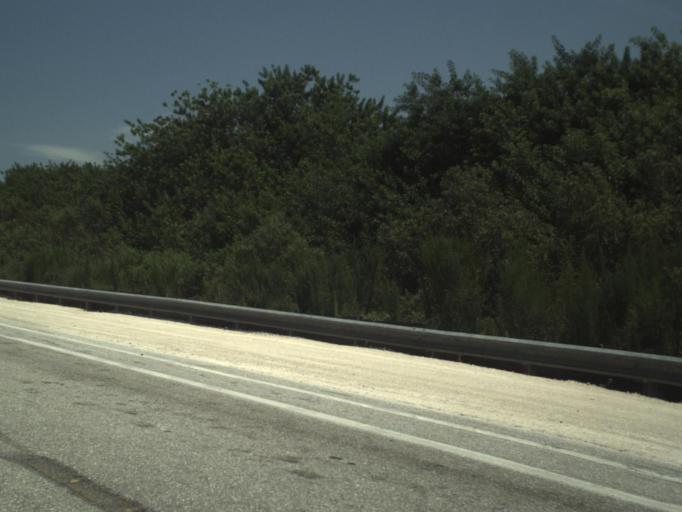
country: US
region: Florida
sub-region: Okeechobee County
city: Taylor Creek
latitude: 27.1298
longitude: -80.6332
